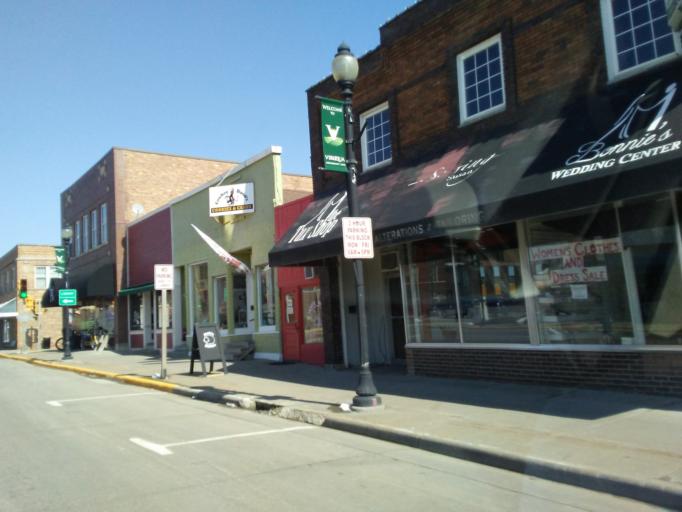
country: US
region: Wisconsin
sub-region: Vernon County
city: Viroqua
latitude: 43.5549
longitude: -90.8893
